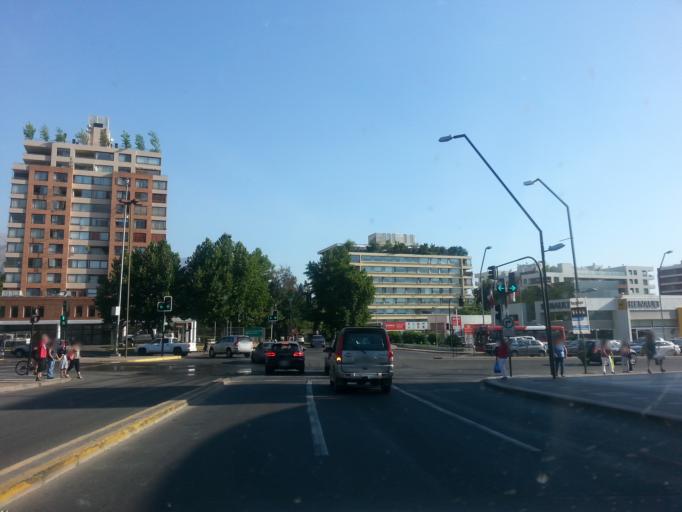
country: CL
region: Santiago Metropolitan
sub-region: Provincia de Santiago
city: Villa Presidente Frei, Nunoa, Santiago, Chile
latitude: -33.3702
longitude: -70.5115
